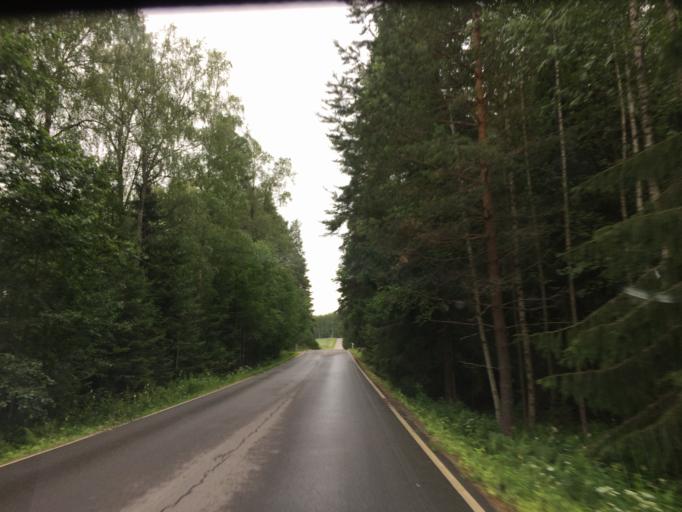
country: FI
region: Haeme
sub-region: Haemeenlinna
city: Janakkala
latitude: 60.8510
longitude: 24.5269
